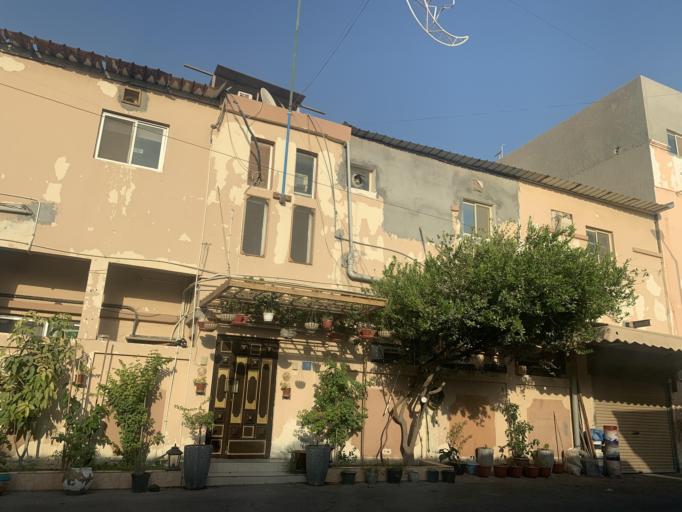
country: BH
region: Muharraq
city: Al Muharraq
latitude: 26.2854
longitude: 50.6274
